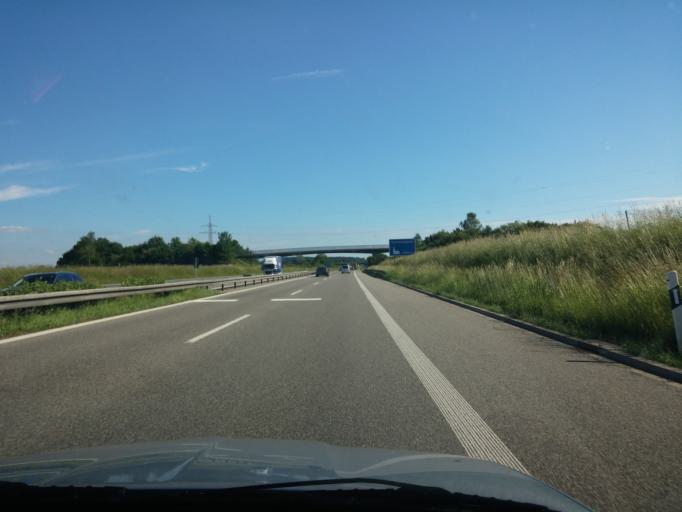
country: DE
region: Baden-Wuerttemberg
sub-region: Tuebingen Region
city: Leutkirch im Allgau
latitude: 47.8311
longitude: 9.9914
